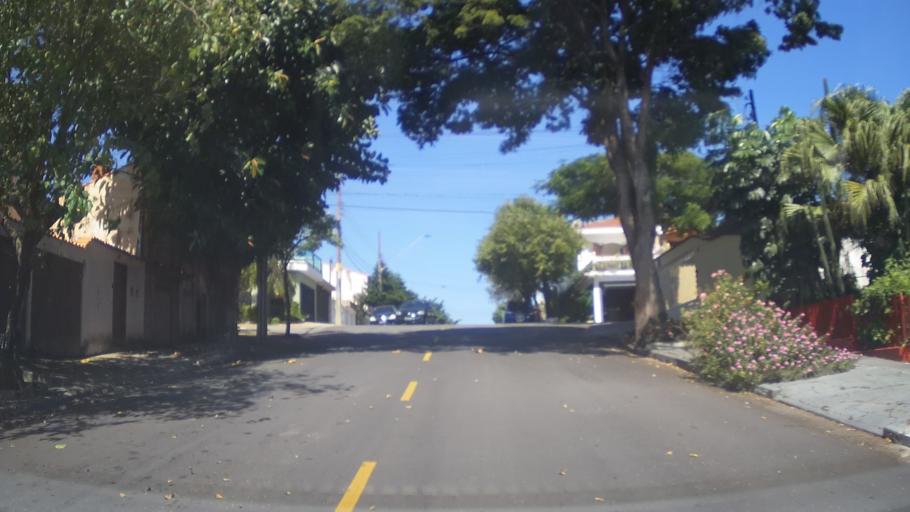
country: BR
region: Sao Paulo
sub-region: Sao Caetano Do Sul
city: Sao Caetano do Sul
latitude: -23.6359
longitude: -46.5792
